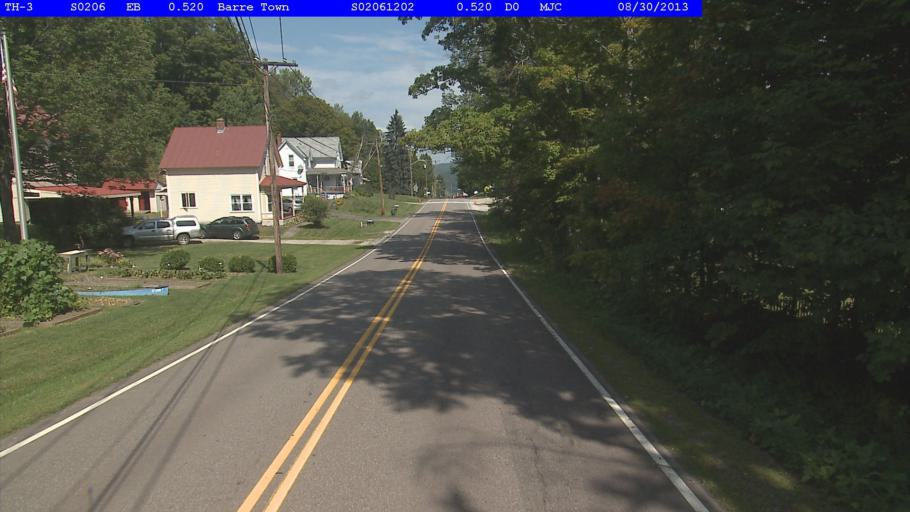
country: US
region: Vermont
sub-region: Washington County
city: South Barre
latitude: 44.1523
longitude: -72.4751
